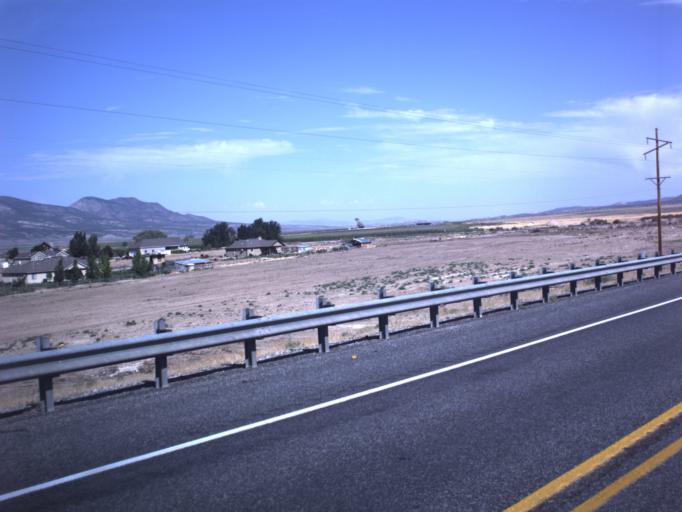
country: US
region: Utah
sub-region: Sanpete County
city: Gunnison
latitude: 39.2266
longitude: -111.8479
